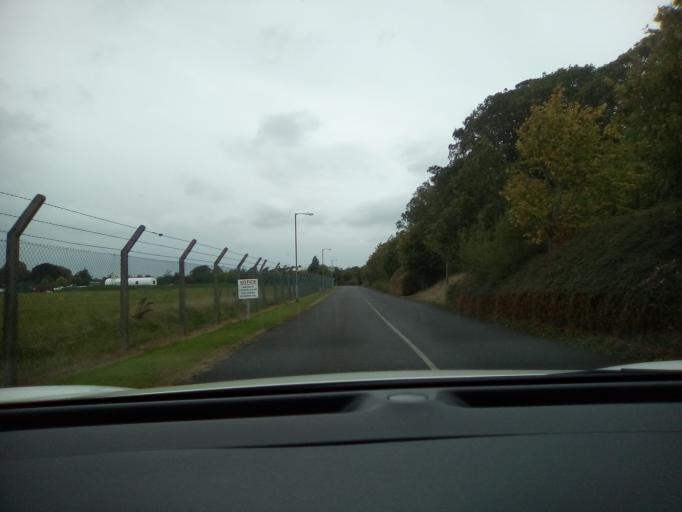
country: IE
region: Leinster
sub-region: Kildare
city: Leixlip
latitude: 53.3566
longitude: -6.4850
